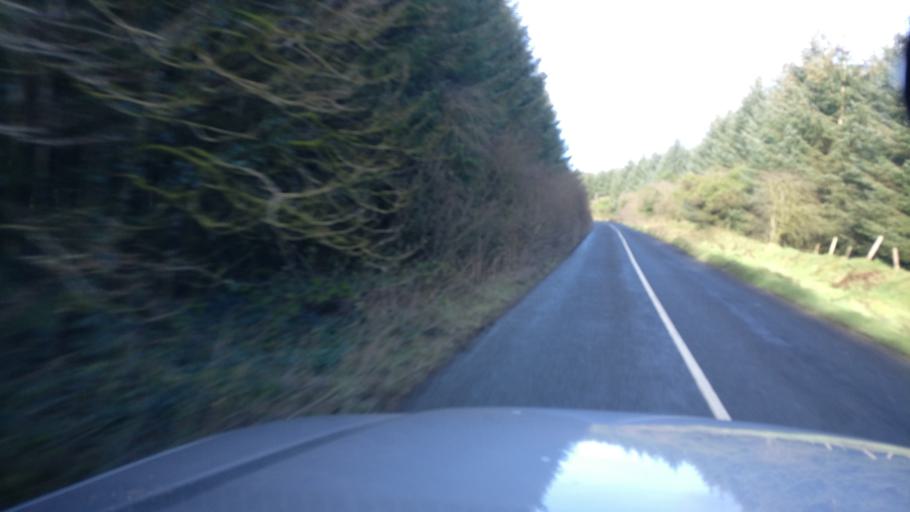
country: IE
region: Leinster
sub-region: Laois
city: Stradbally
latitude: 52.9114
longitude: -7.1833
